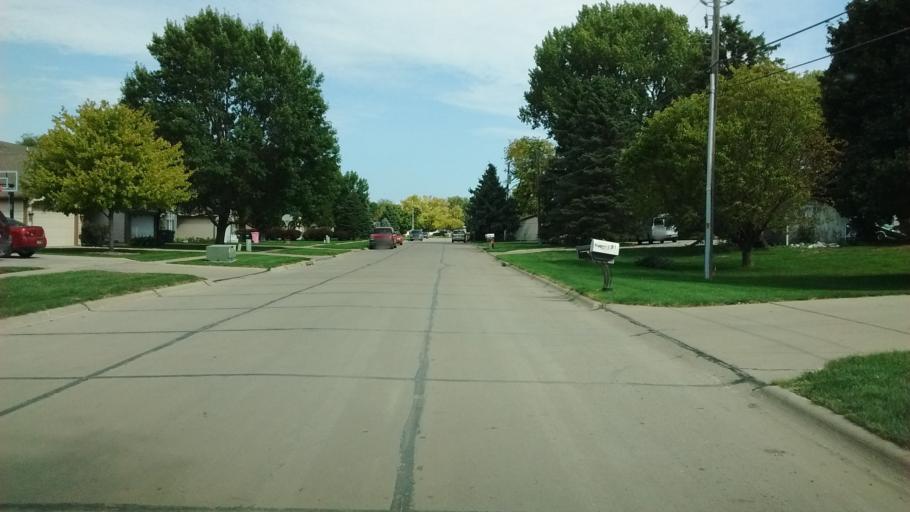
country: US
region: South Dakota
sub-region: Union County
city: North Sioux City
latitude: 42.5429
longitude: -96.5250
